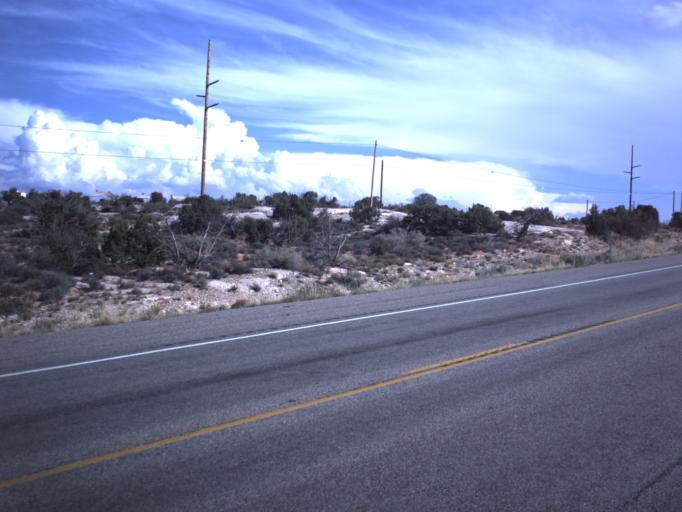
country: US
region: Utah
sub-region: Grand County
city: Moab
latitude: 38.6854
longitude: -109.6952
